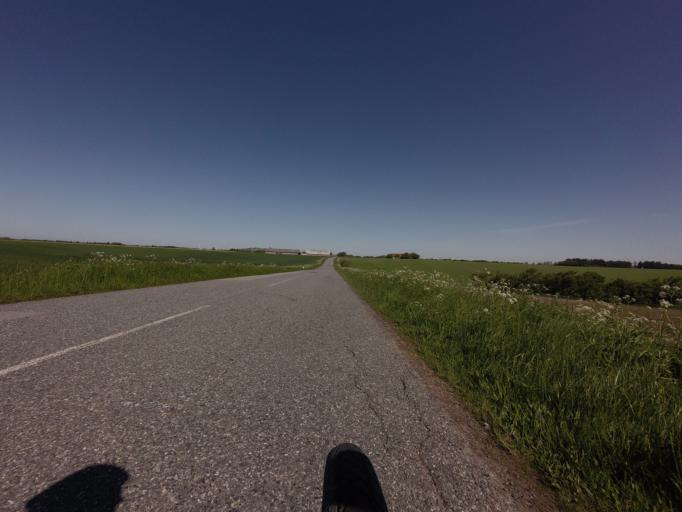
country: DK
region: North Denmark
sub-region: Hjorring Kommune
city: Hjorring
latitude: 57.4406
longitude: 9.9000
